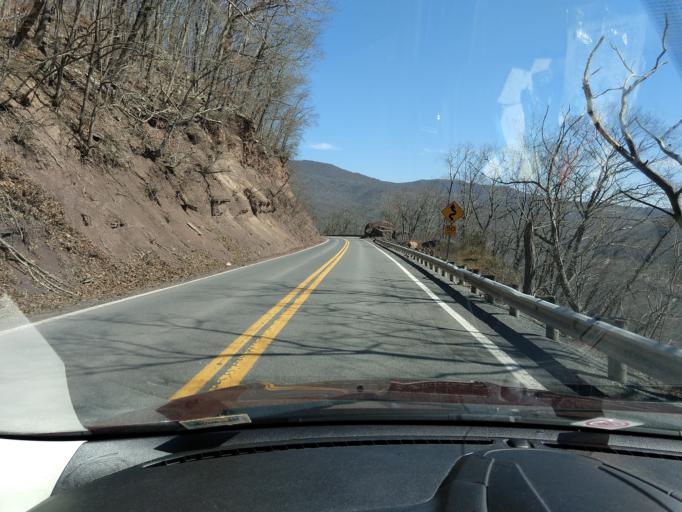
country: US
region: West Virginia
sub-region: Summers County
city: Hinton
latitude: 37.7375
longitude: -80.9114
